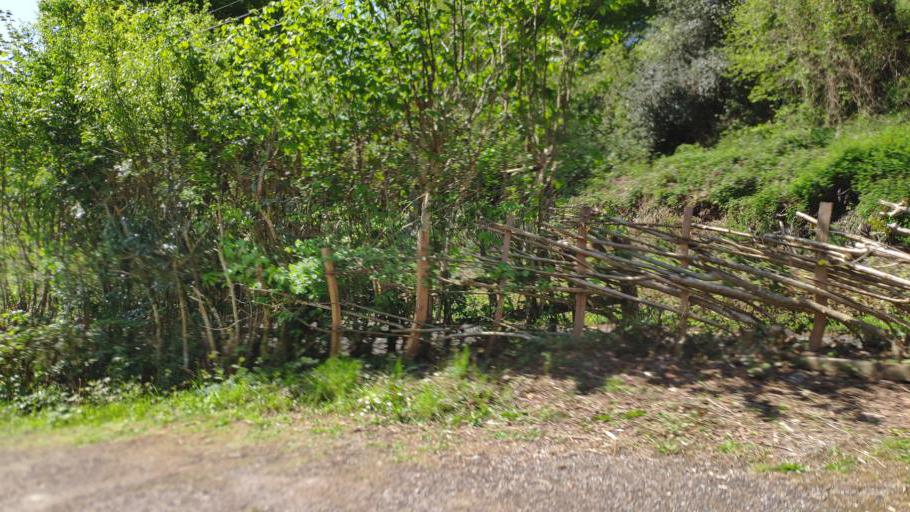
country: IE
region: Munster
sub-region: County Cork
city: Blarney
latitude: 51.9442
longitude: -8.5660
